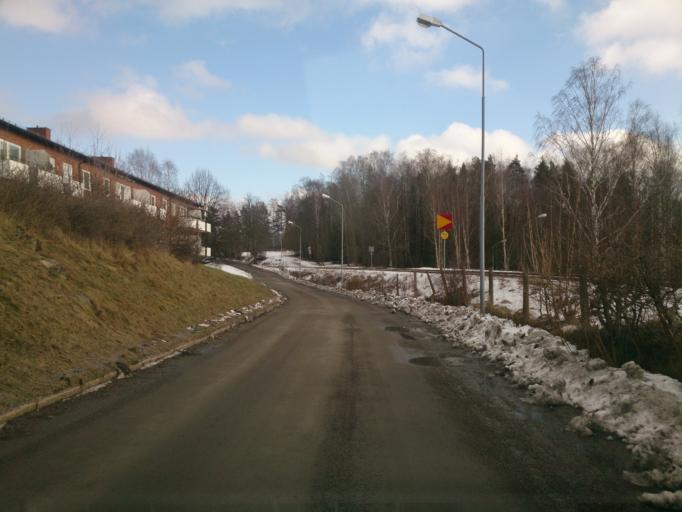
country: SE
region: OEstergoetland
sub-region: Atvidabergs Kommun
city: Atvidaberg
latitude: 58.2022
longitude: 16.0085
